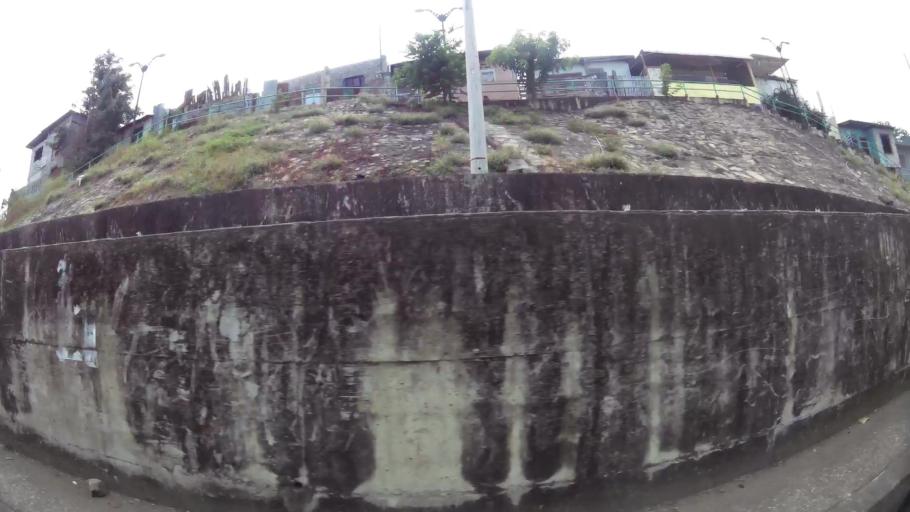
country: EC
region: Guayas
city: Santa Lucia
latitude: -2.1334
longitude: -79.9440
